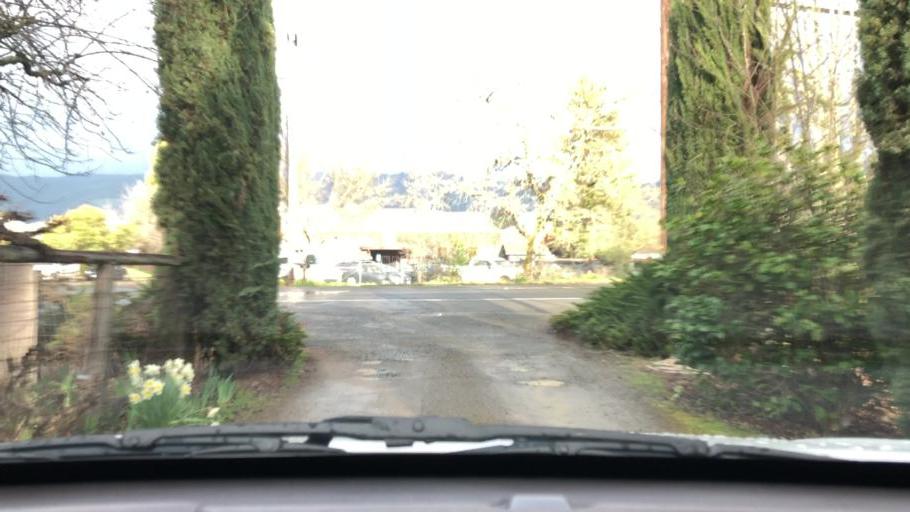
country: US
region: California
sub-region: Mendocino County
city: Talmage
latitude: 39.1104
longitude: -123.1974
